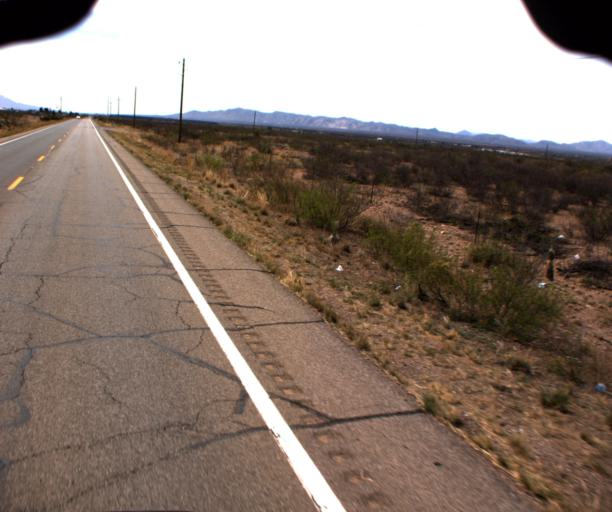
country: US
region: Arizona
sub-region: Cochise County
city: Pirtleville
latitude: 31.3828
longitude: -109.5793
